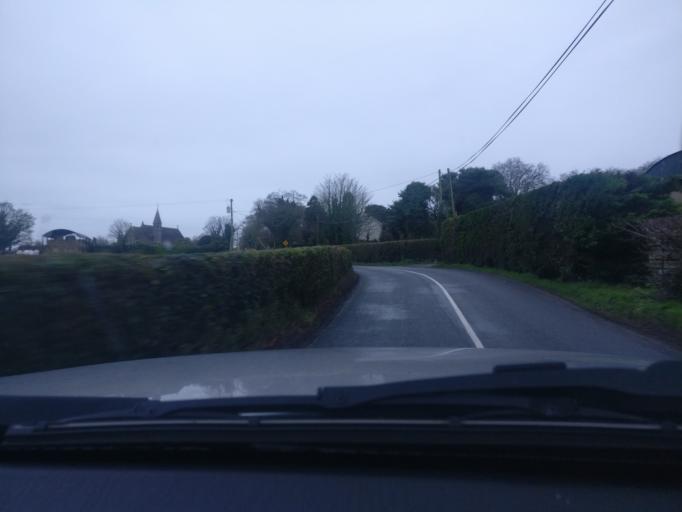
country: IE
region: Leinster
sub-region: An Mhi
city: Dunshaughlin
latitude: 53.4924
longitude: -6.6051
